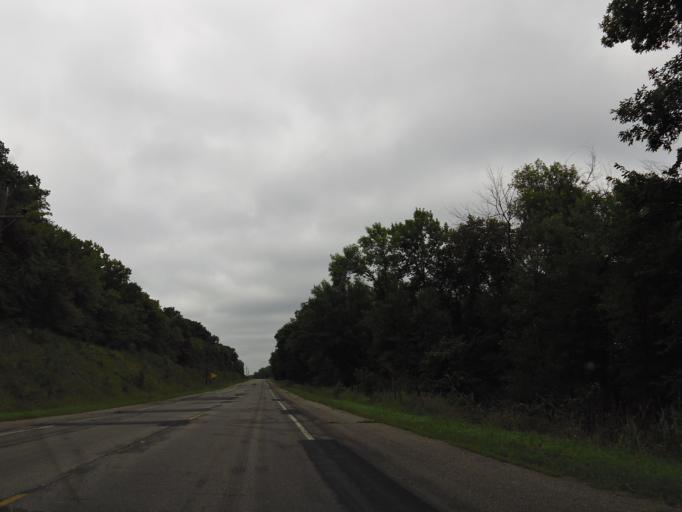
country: US
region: Minnesota
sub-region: Chippewa County
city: Montevideo
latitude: 44.8745
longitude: -95.6434
